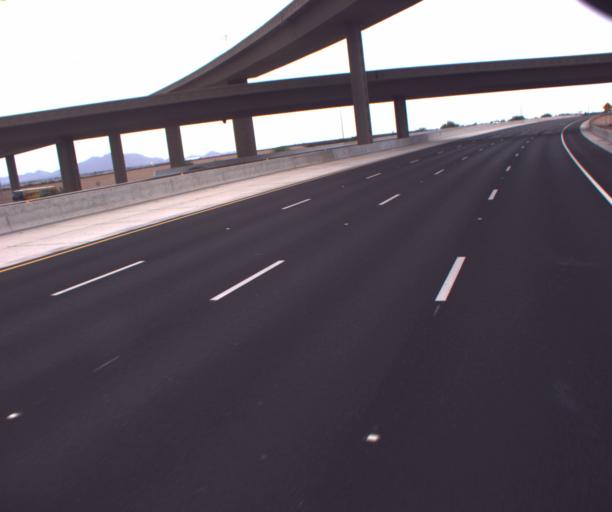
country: US
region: Arizona
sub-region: Maricopa County
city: Queen Creek
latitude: 33.3327
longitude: -111.6502
